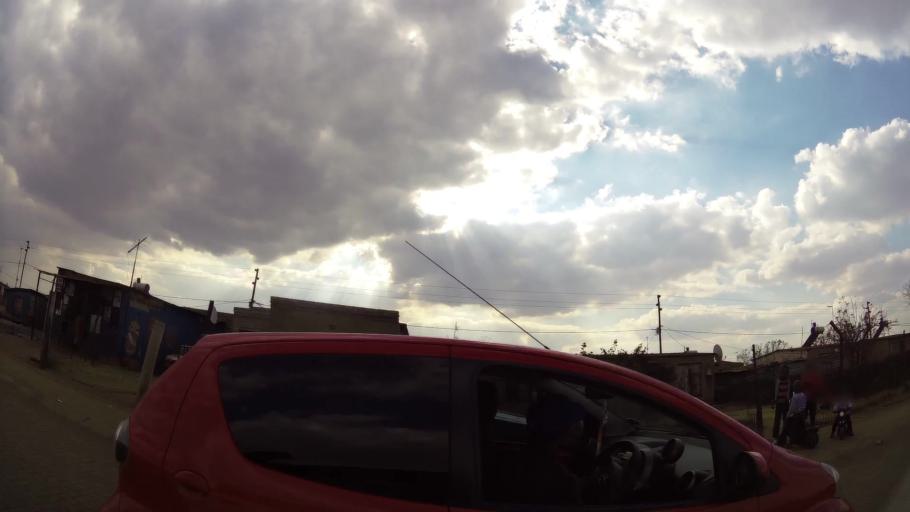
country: ZA
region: Mpumalanga
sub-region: Nkangala District Municipality
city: Delmas
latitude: -26.1396
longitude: 28.6960
